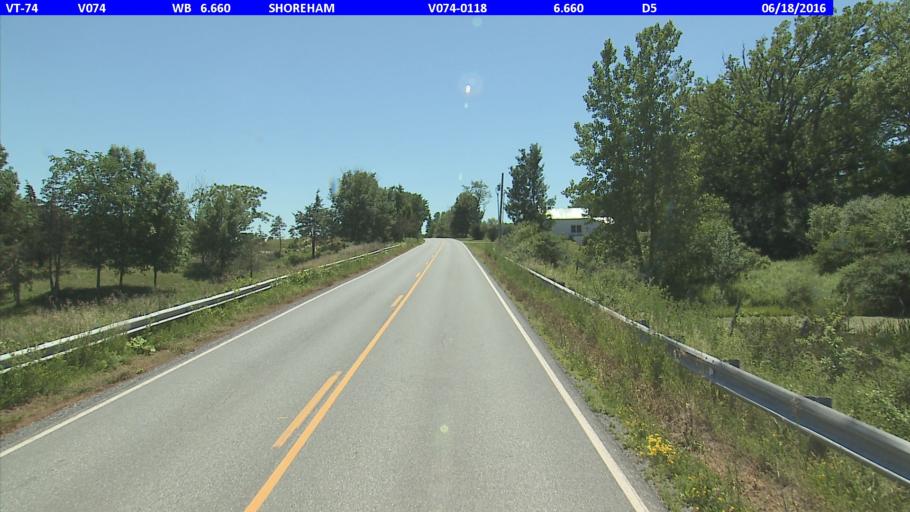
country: US
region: New York
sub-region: Essex County
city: Ticonderoga
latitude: 43.9156
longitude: -73.2958
